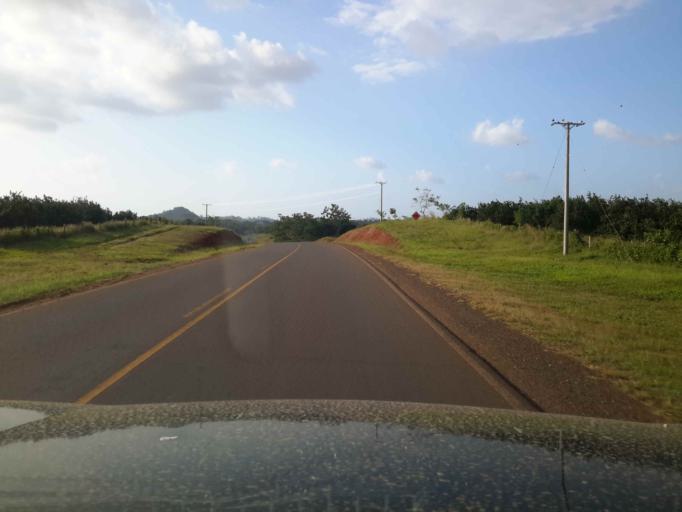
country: NI
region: Rio San Juan
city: San Carlos
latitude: 11.1652
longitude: -84.6653
